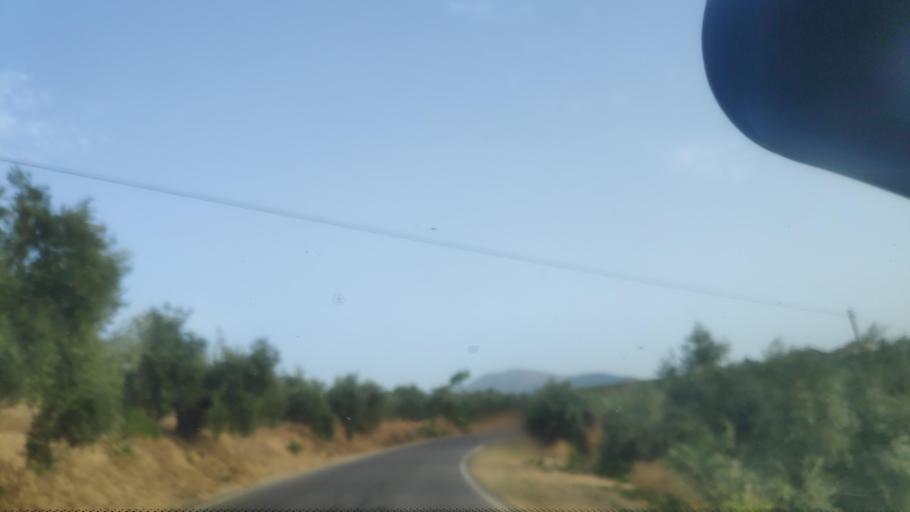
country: ES
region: Andalusia
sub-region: Provincia de Jaen
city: Torres
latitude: 37.8190
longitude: -3.5328
